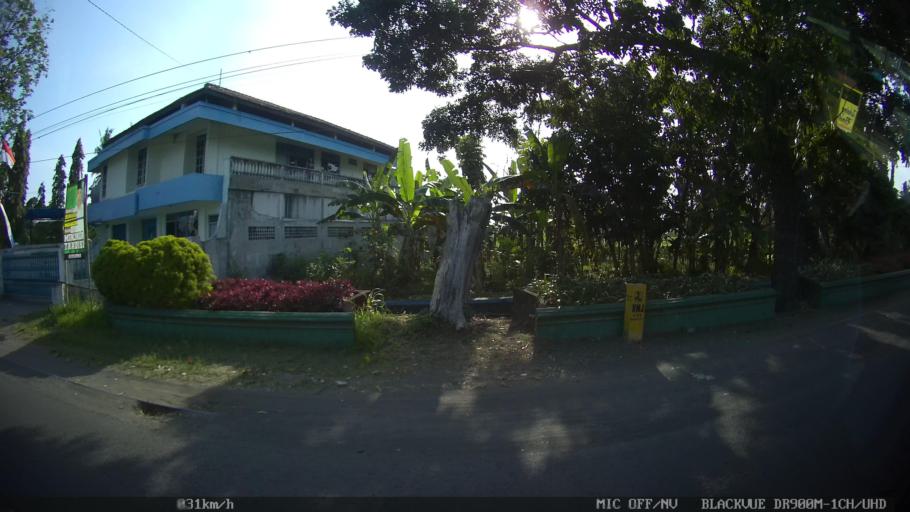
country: ID
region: Daerah Istimewa Yogyakarta
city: Bantul
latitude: -7.9011
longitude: 110.3217
